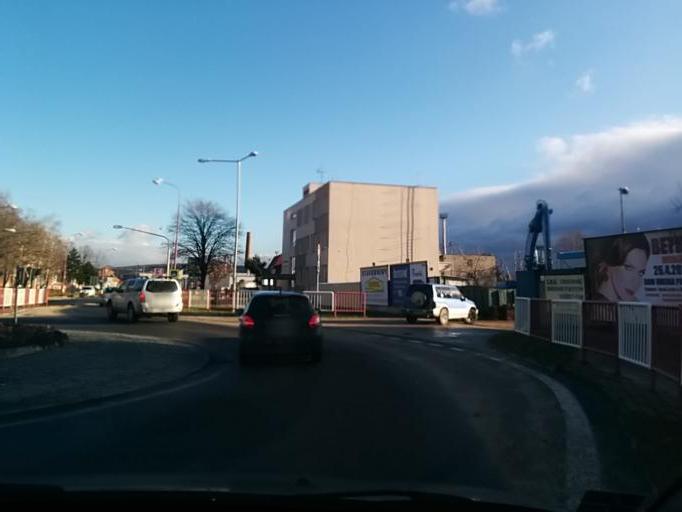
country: SK
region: Trenciansky
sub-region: Okres Nove Mesto nad Vahom
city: Nove Mesto nad Vahom
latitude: 48.7548
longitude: 17.8359
